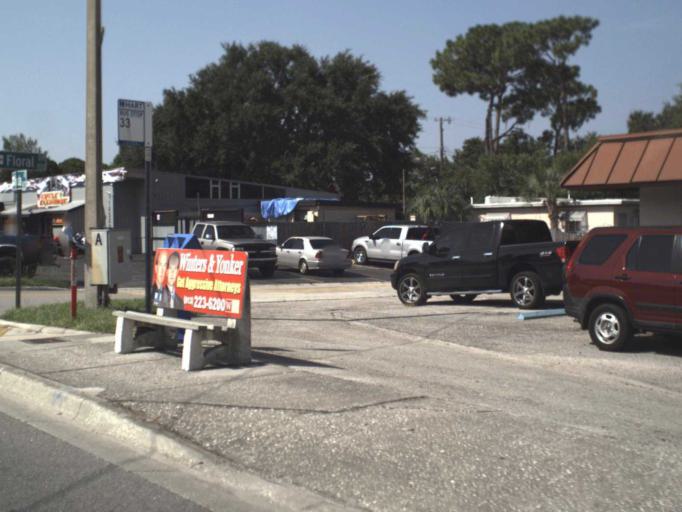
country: US
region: Florida
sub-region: Hillsborough County
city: Lake Magdalene
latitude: 28.0805
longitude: -82.4596
